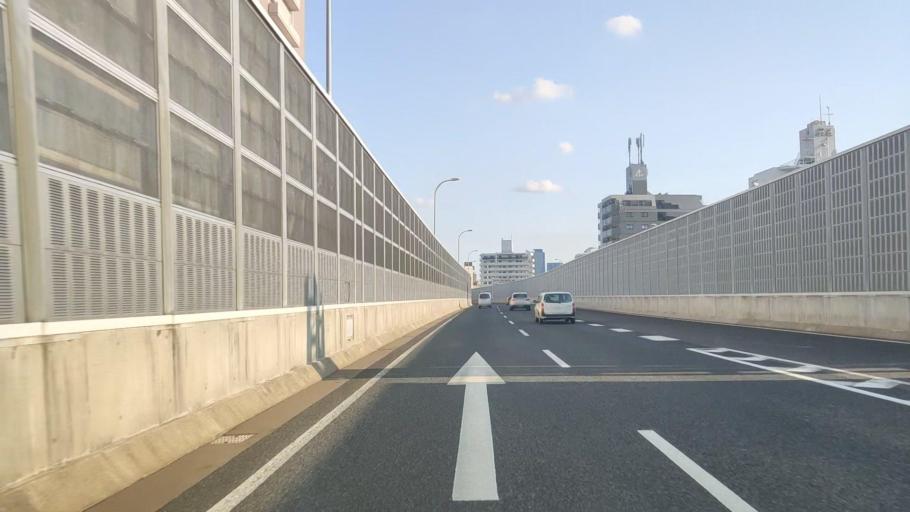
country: JP
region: Aichi
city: Nagoya-shi
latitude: 35.1985
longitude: 136.8908
